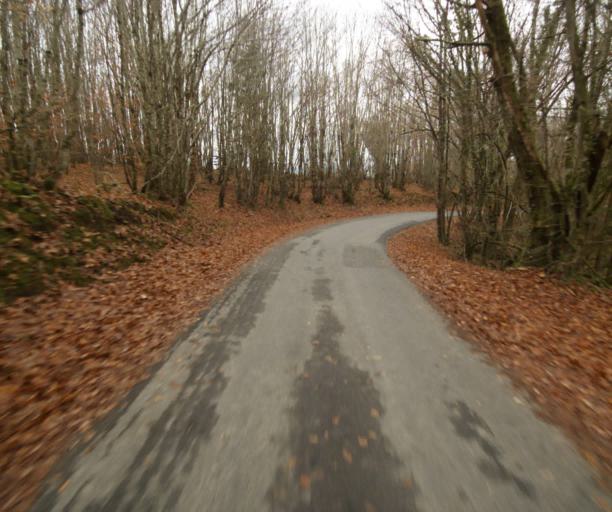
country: FR
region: Limousin
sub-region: Departement de la Correze
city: Laguenne
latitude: 45.2334
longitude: 1.7539
